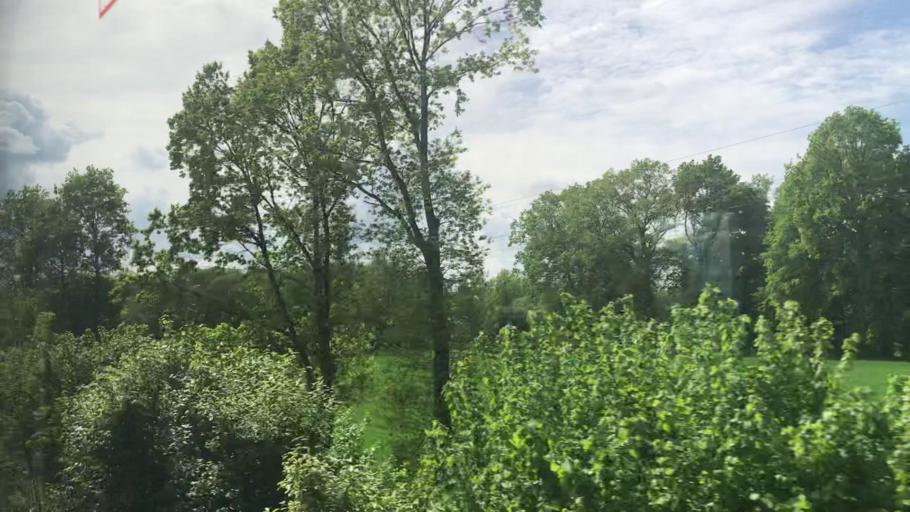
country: PL
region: Lower Silesian Voivodeship
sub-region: Powiat swidnicki
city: Jaworzyna Slaska
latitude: 50.8916
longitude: 16.3971
